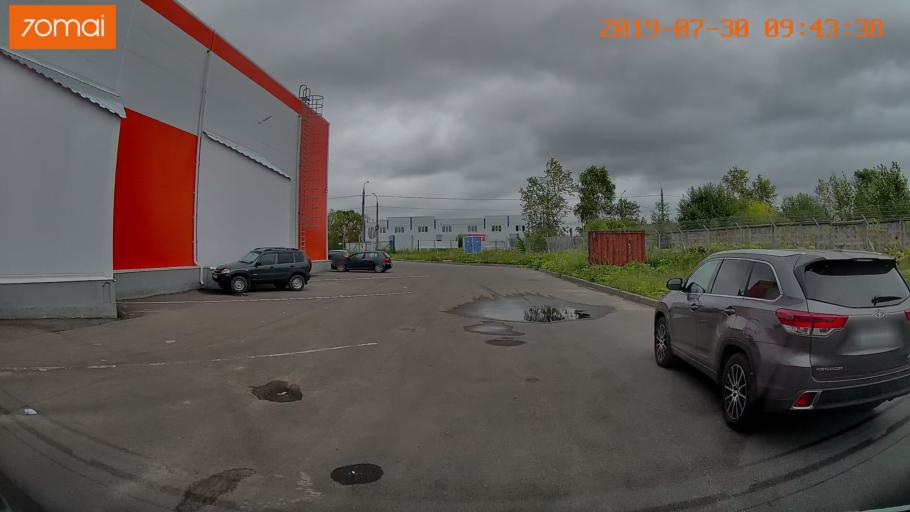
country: RU
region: Ivanovo
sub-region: Gorod Ivanovo
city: Ivanovo
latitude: 56.9495
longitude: 40.9575
